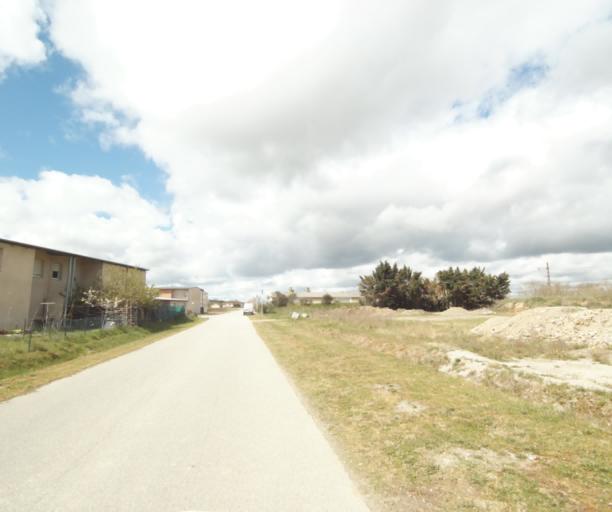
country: FR
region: Midi-Pyrenees
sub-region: Departement de l'Ariege
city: Saverdun
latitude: 43.2347
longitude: 1.5865
